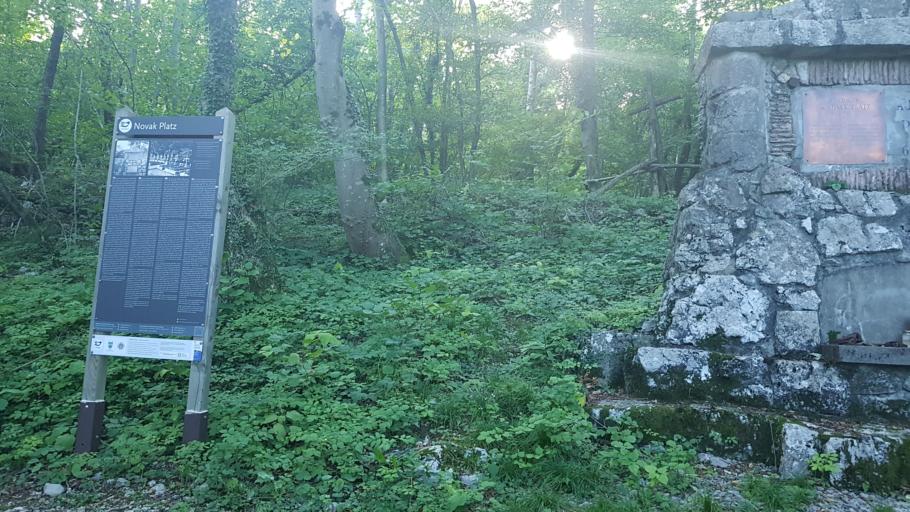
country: SI
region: Kanal
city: Deskle
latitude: 46.0229
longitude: 13.6223
